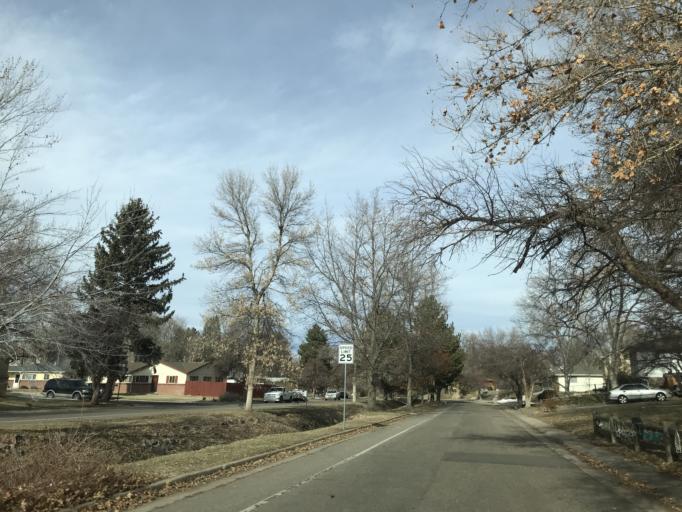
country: US
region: Colorado
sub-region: Arapahoe County
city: Littleton
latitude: 39.6052
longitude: -105.0097
